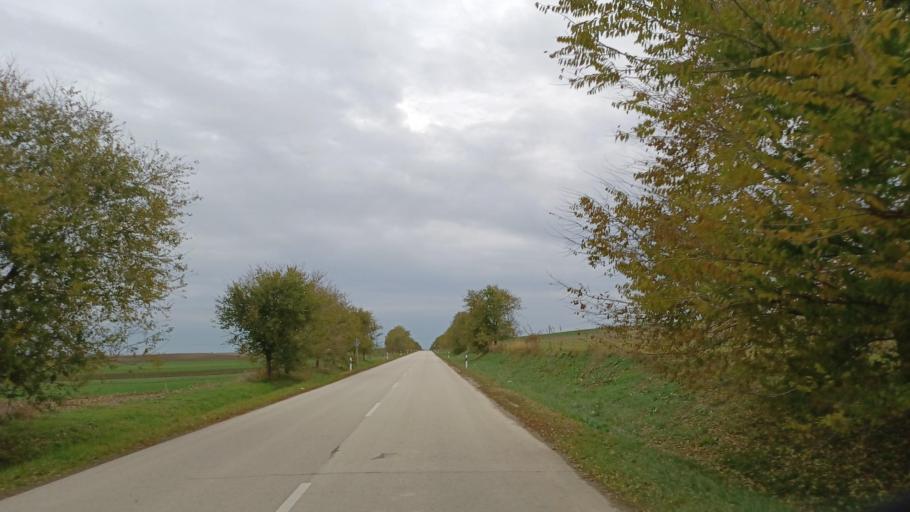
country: HU
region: Tolna
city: Nagydorog
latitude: 46.6770
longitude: 18.6005
